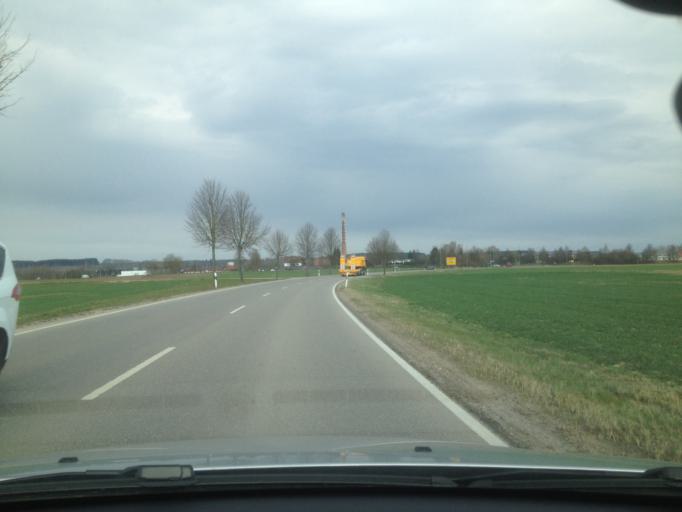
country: DE
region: Bavaria
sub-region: Swabia
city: Bobingen
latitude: 48.2572
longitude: 10.8242
